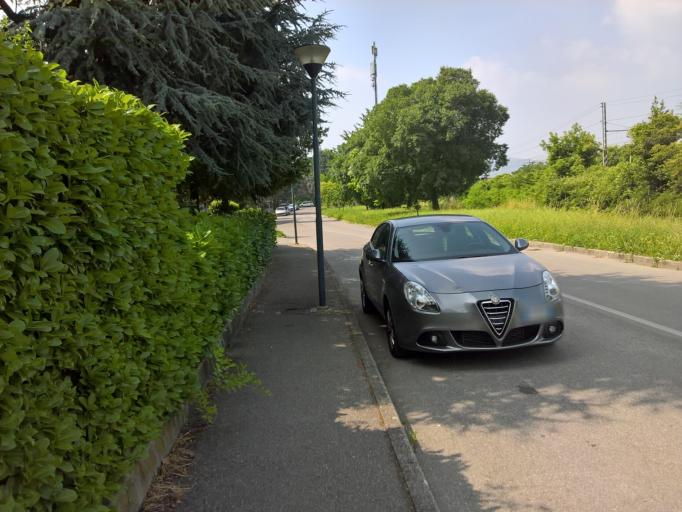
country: IT
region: Veneto
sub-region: Provincia di Padova
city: Battaglia Terme
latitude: 45.2927
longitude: 11.7794
